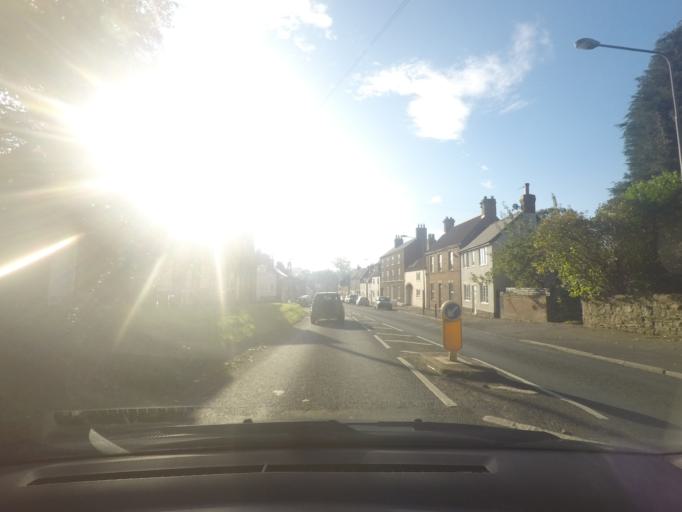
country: GB
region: England
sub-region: East Riding of Yorkshire
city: South Cave
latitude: 53.7709
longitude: -0.6012
